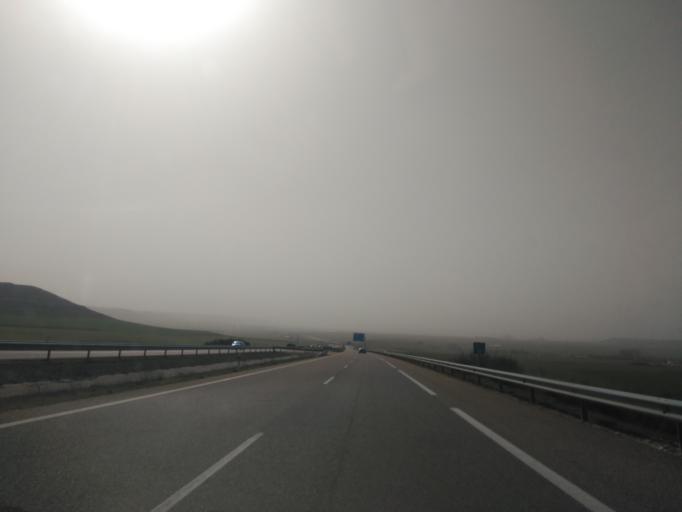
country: ES
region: Castille and Leon
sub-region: Provincia de Palencia
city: Fuentes de Valdepero
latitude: 42.0861
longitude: -4.4884
